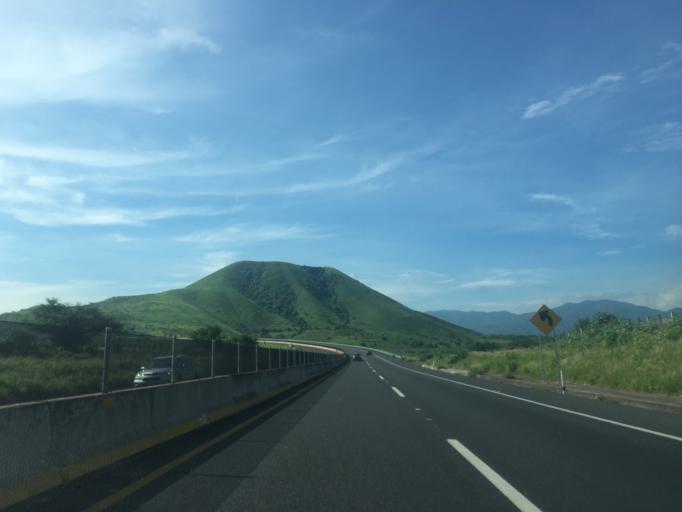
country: MX
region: Nayarit
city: Jala
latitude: 21.0636
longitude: -104.4173
